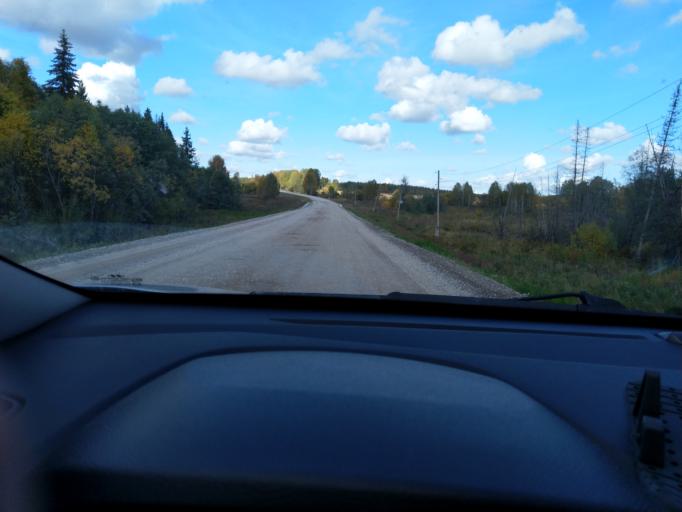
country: RU
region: Perm
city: Usol'ye
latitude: 59.4658
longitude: 56.3704
